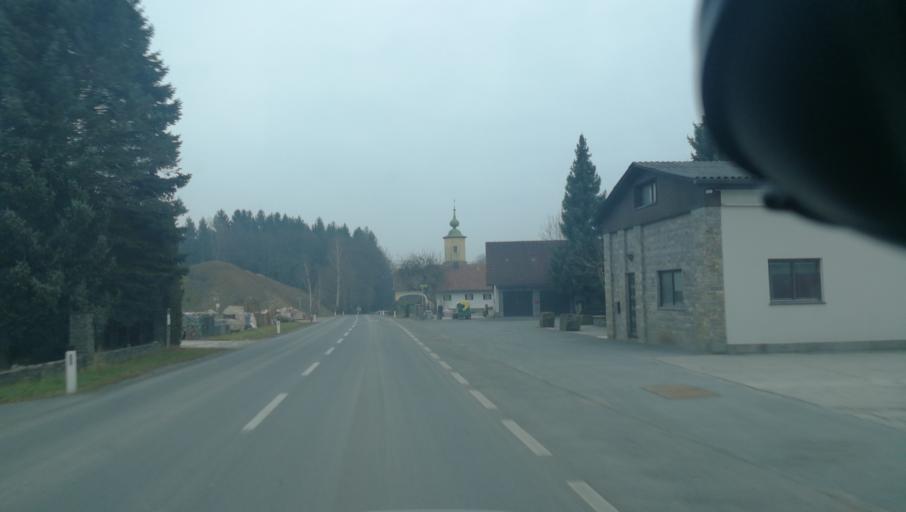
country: AT
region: Styria
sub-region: Politischer Bezirk Deutschlandsberg
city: Stainz
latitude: 46.9029
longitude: 15.2434
